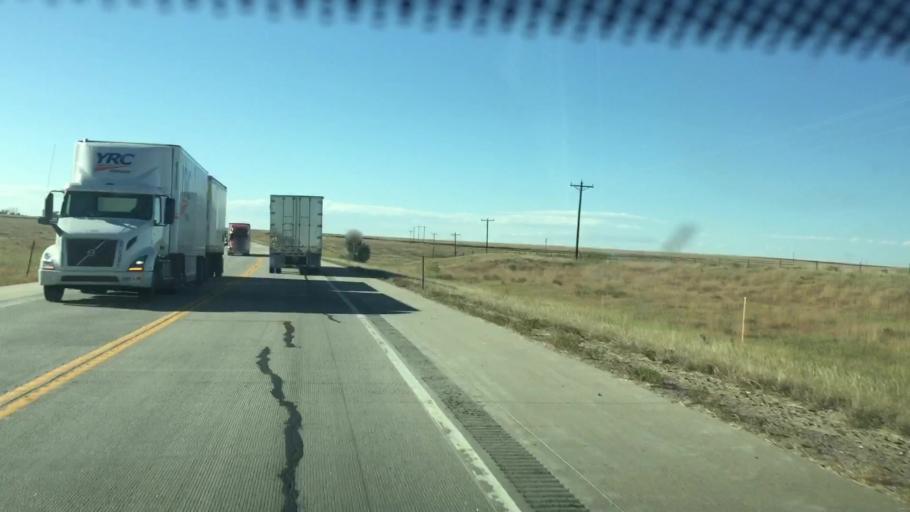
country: US
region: Colorado
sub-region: Kiowa County
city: Eads
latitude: 38.8240
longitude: -102.9926
